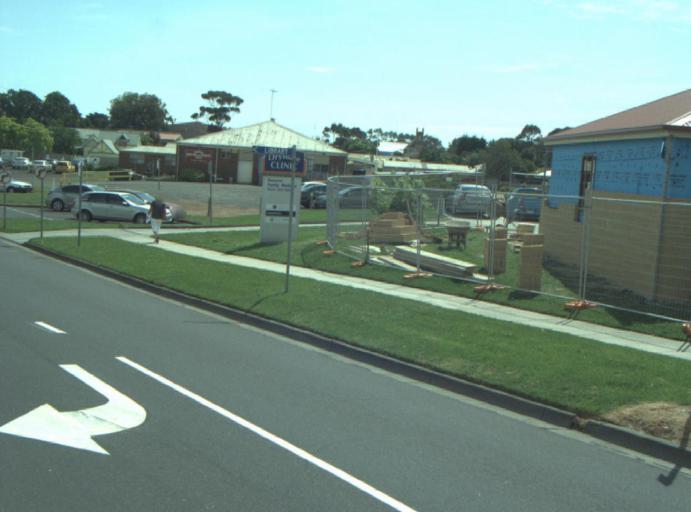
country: AU
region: Victoria
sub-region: Greater Geelong
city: Clifton Springs
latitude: -38.1720
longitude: 144.5712
